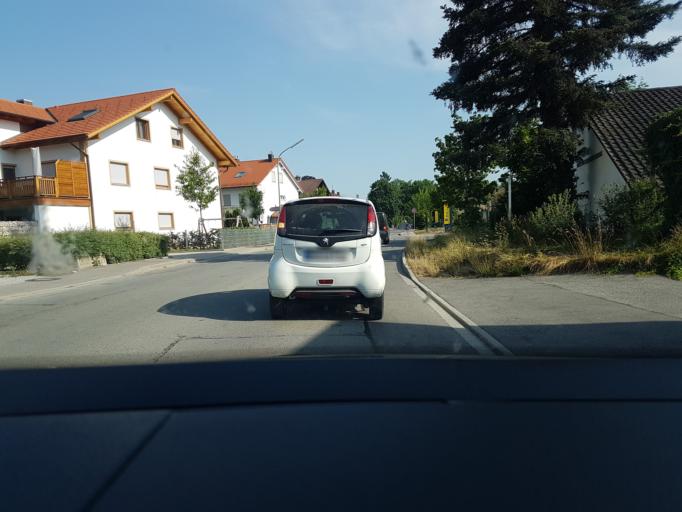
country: DE
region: Bavaria
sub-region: Upper Bavaria
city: Rosenheim
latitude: 47.8411
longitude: 12.1124
